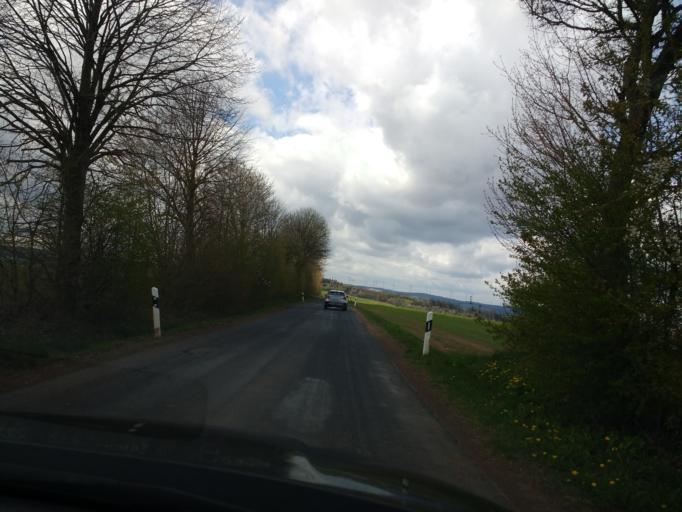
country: DE
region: Rheinland-Pfalz
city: Esch
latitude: 50.3627
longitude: 6.6026
